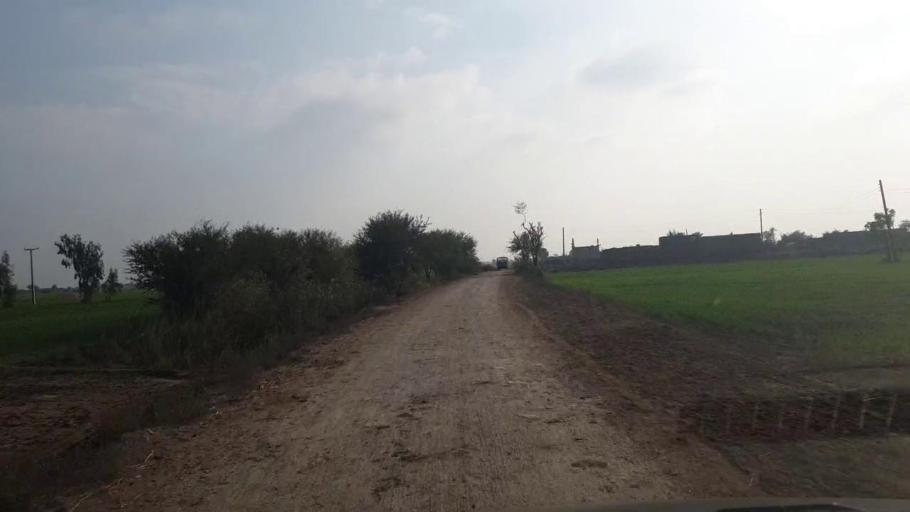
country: PK
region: Sindh
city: Shahdadpur
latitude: 25.8714
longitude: 68.6635
